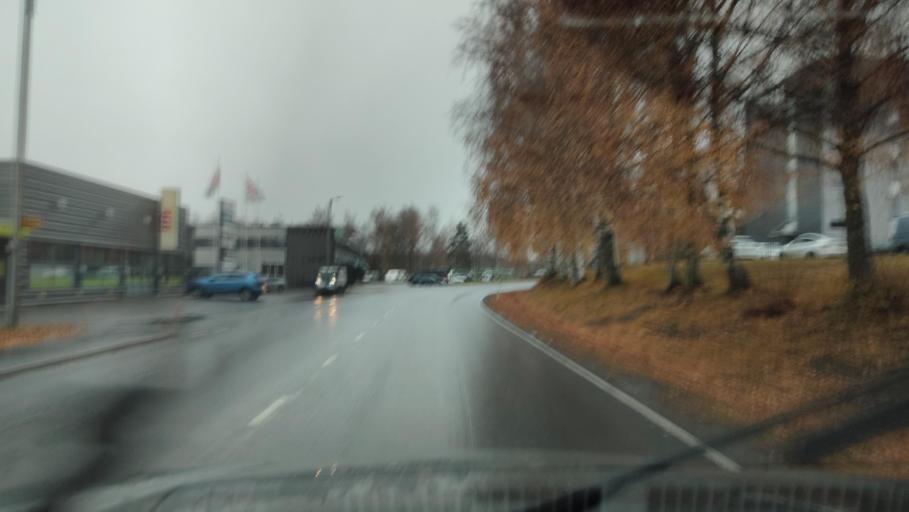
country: FI
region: Ostrobothnia
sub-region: Vaasa
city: Korsholm
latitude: 63.0935
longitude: 21.6543
